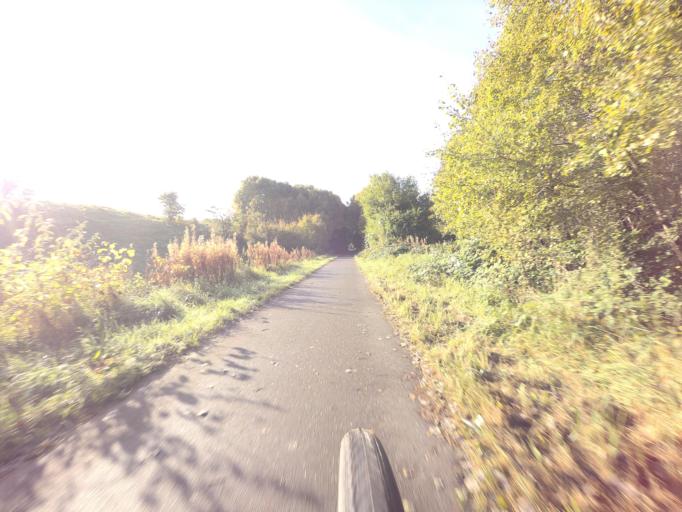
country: DK
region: Central Jutland
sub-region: Viborg Kommune
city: Bjerringbro
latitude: 56.4668
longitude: 9.5897
